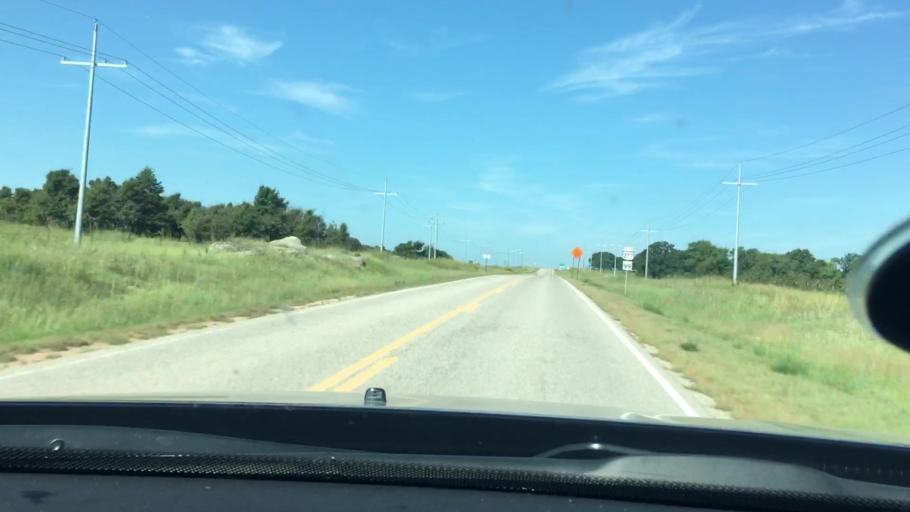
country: US
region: Oklahoma
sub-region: Johnston County
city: Tishomingo
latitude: 34.3613
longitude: -96.6256
